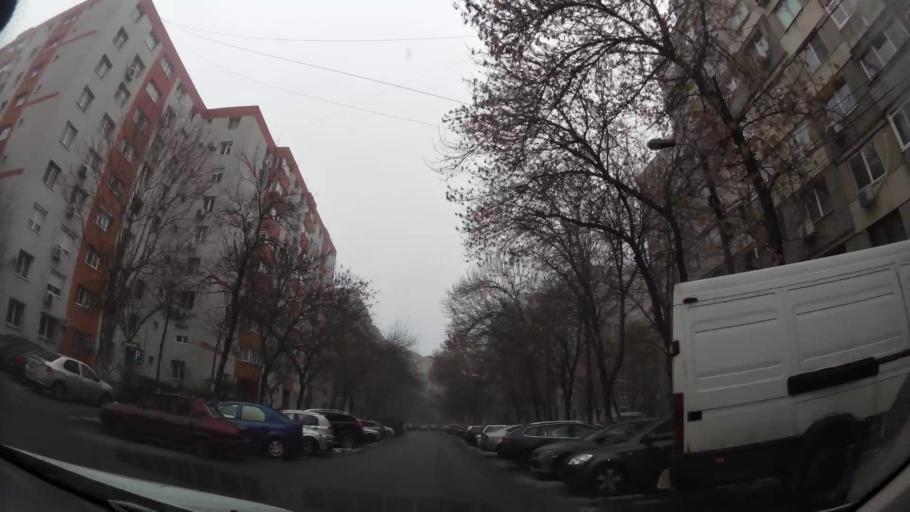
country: RO
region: Ilfov
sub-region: Comuna Chiajna
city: Rosu
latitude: 44.4556
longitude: 26.0499
